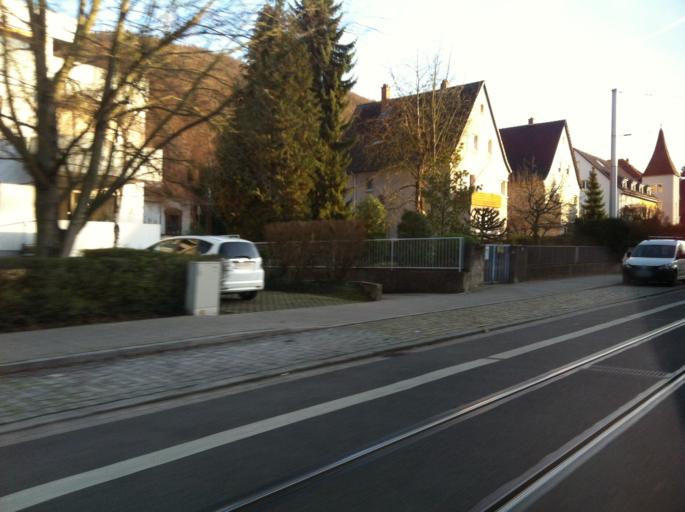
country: DE
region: Baden-Wuerttemberg
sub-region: Karlsruhe Region
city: Heidelberg
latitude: 49.3908
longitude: 8.6904
